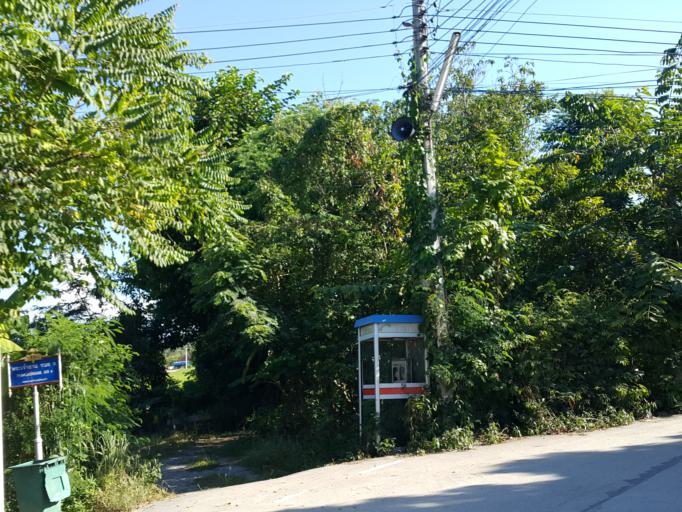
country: TH
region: Chiang Mai
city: San Kamphaeng
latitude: 18.7688
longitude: 99.0965
